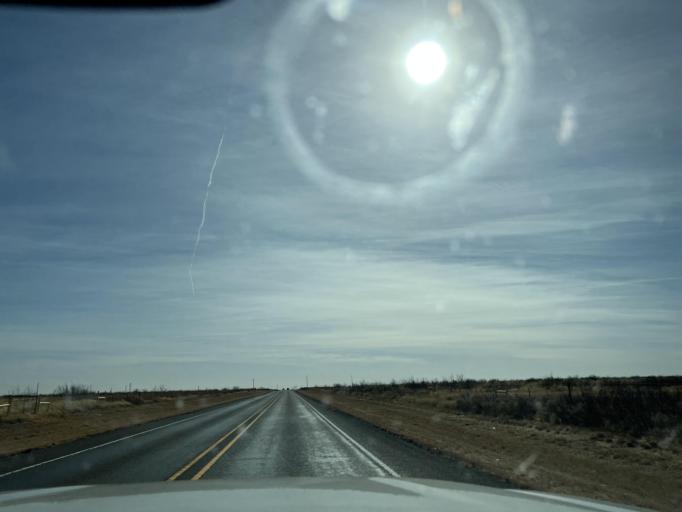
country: US
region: Texas
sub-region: Andrews County
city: Andrews
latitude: 32.4325
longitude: -102.4383
